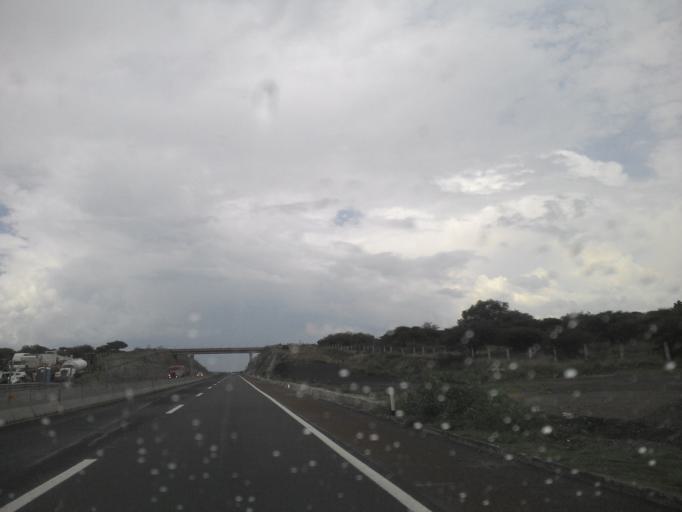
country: MX
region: Hidalgo
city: Tula de Allende
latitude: 20.0642
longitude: -99.3840
